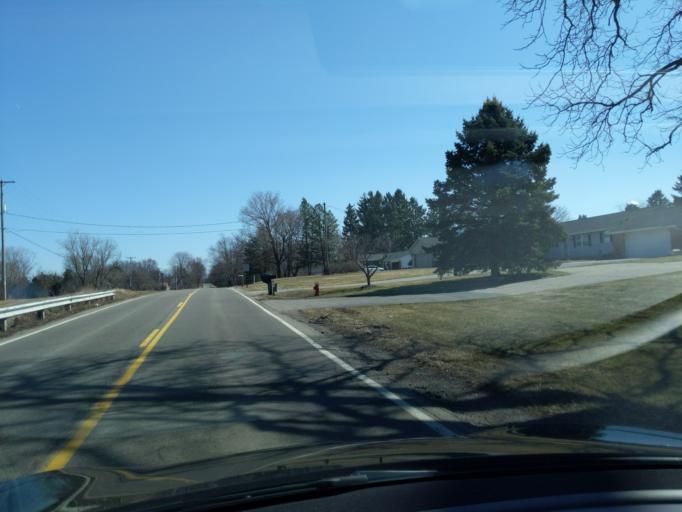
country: US
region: Michigan
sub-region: Ingham County
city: Holt
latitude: 42.6547
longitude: -84.4960
